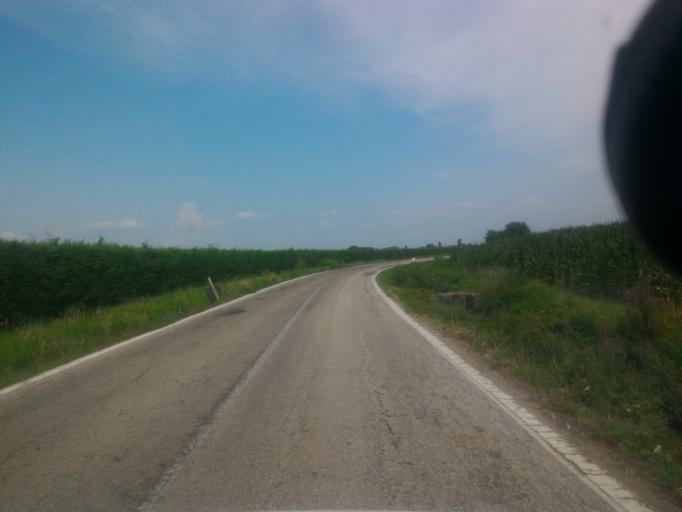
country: IT
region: Piedmont
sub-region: Provincia di Torino
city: Vigone
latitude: 44.8526
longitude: 7.4584
